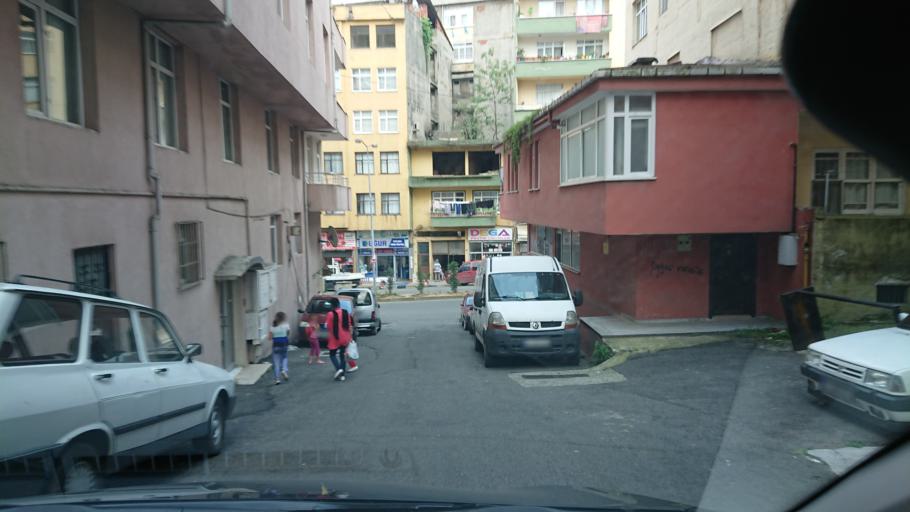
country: TR
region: Rize
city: Rize
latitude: 41.0219
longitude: 40.5184
